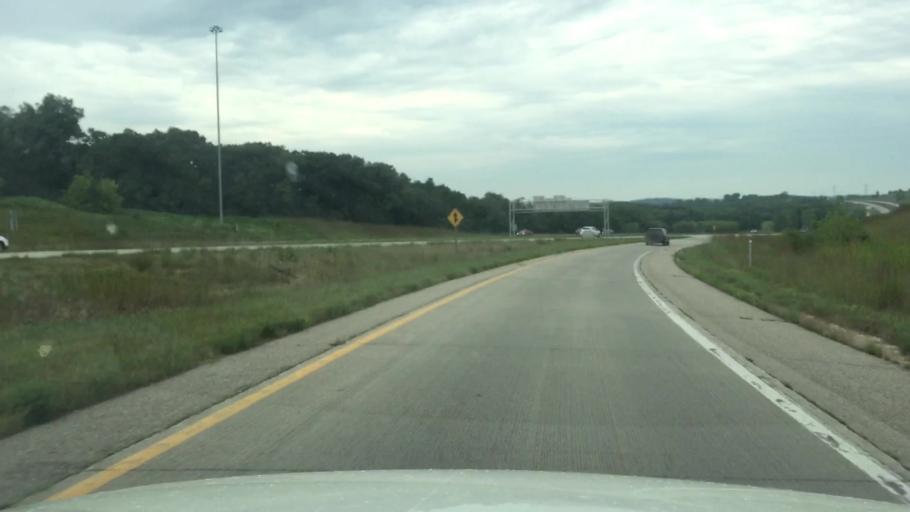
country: US
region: Iowa
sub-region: Warren County
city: Carlisle
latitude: 41.5058
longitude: -93.5775
